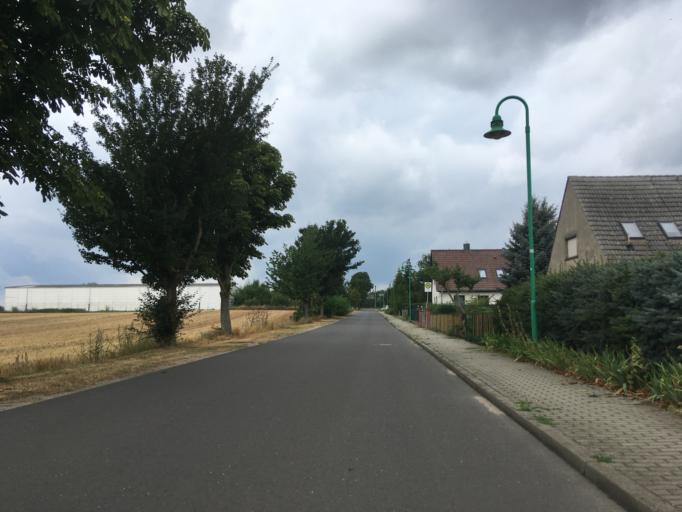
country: DE
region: Brandenburg
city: Angermunde
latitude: 52.9786
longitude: 13.9658
